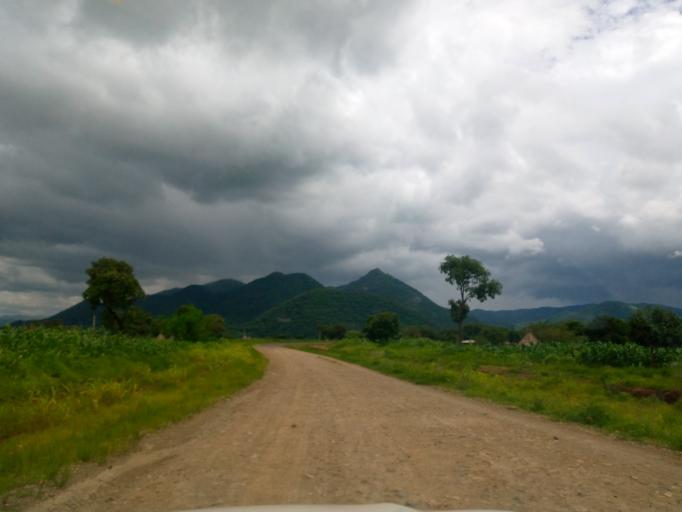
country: ET
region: Oromiya
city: Mendi
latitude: 10.1819
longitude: 35.0925
